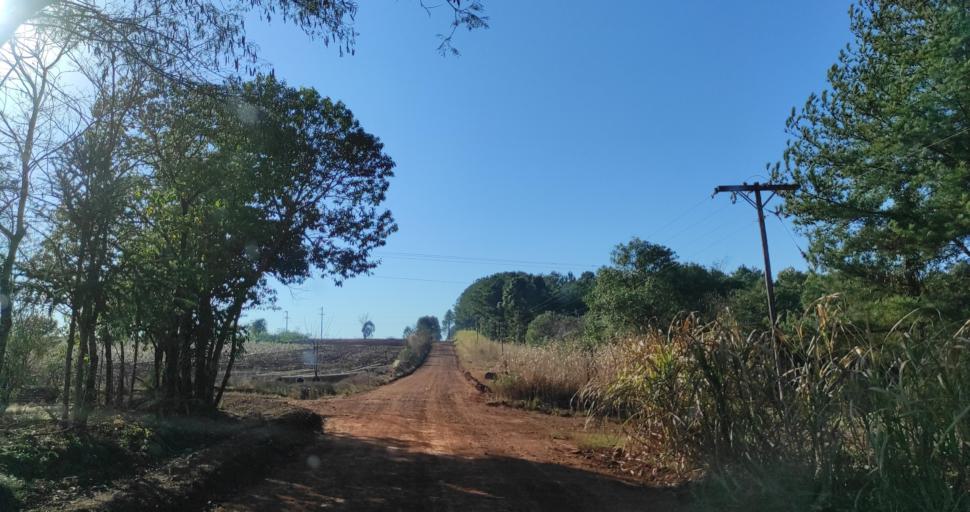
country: AR
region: Misiones
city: Capiovi
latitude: -26.8801
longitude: -55.0170
